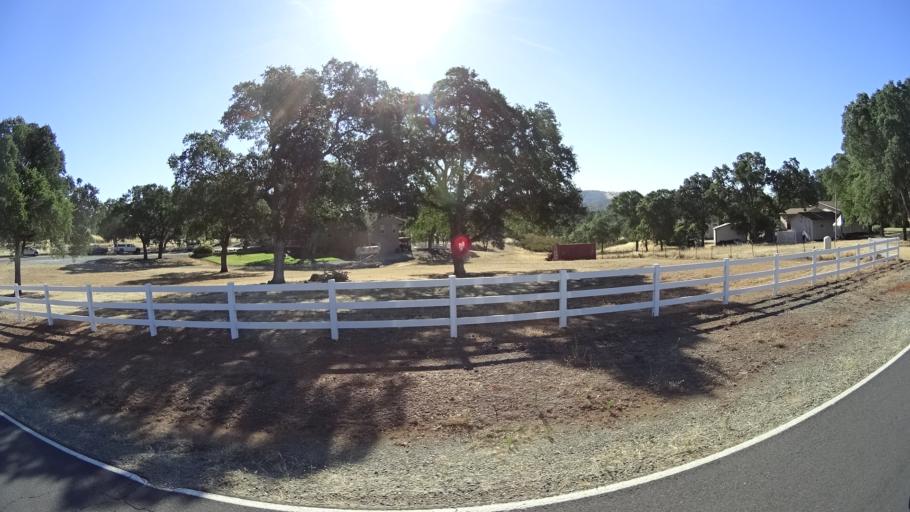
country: US
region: California
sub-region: Calaveras County
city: Rancho Calaveras
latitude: 38.1258
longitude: -120.8616
